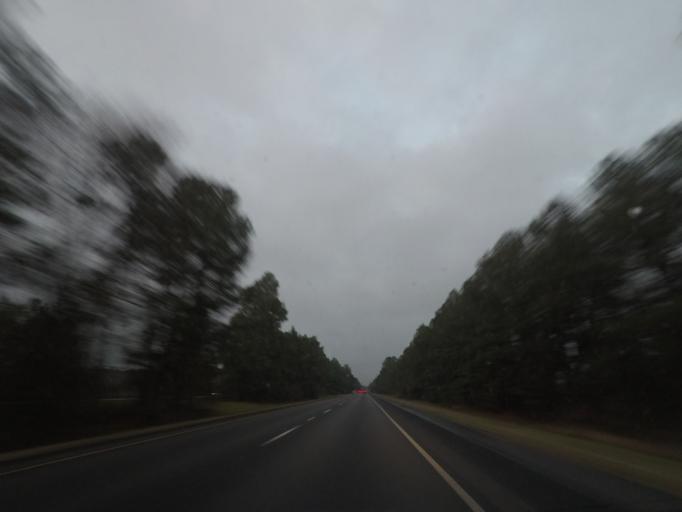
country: US
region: South Carolina
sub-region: Clarendon County
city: Manning
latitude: 33.7807
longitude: -80.1700
